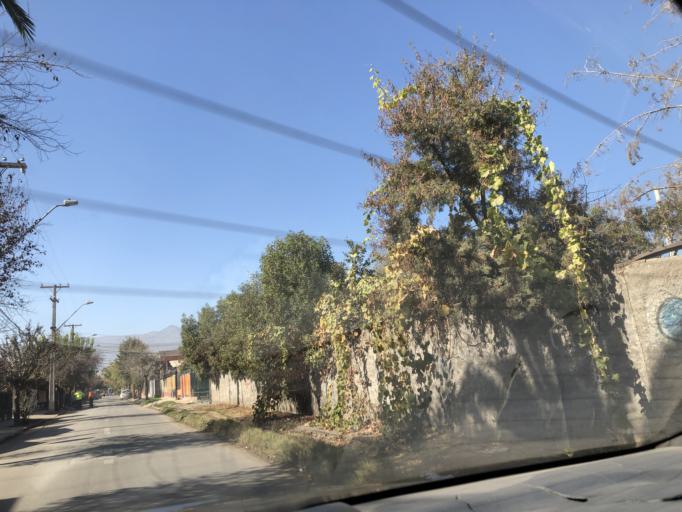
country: CL
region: Santiago Metropolitan
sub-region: Provincia de Cordillera
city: Puente Alto
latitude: -33.5779
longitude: -70.5900
